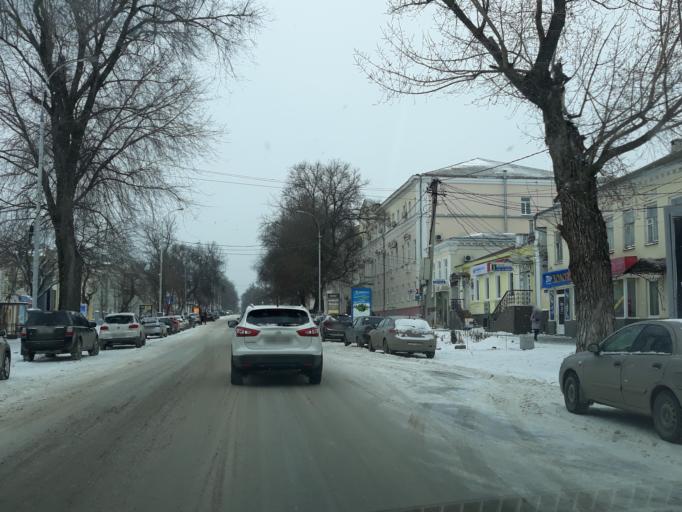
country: RU
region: Rostov
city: Taganrog
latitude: 47.2172
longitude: 38.9263
